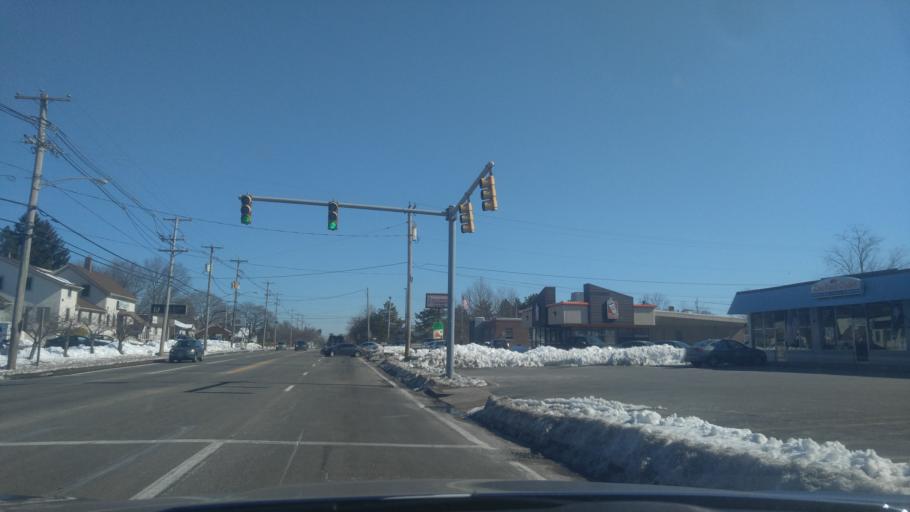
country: US
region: Rhode Island
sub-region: Providence County
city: Cranston
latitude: 41.7519
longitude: -71.4168
